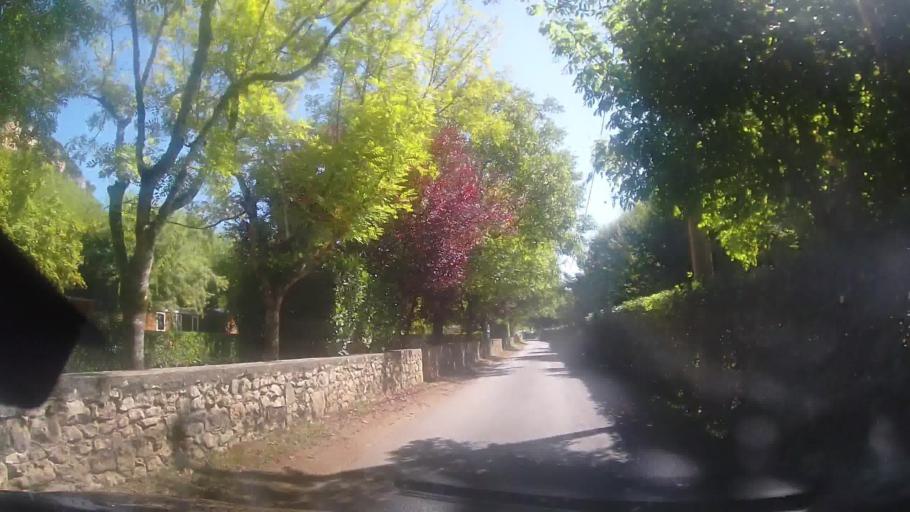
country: FR
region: Aquitaine
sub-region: Departement de la Dordogne
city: Cenac-et-Saint-Julien
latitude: 44.8065
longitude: 1.1575
